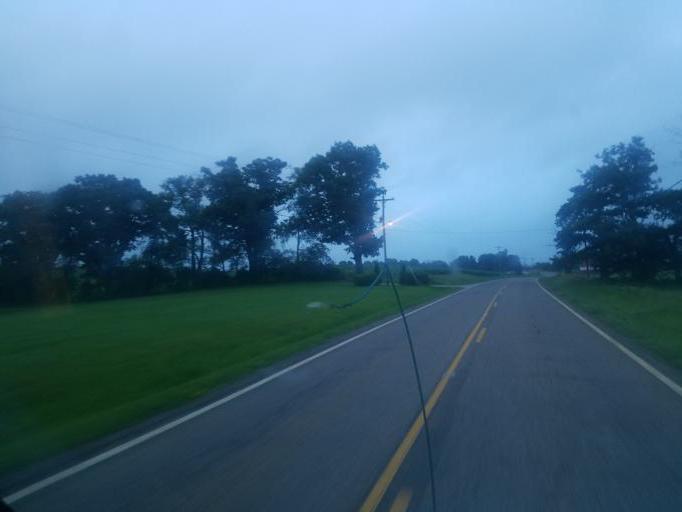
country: US
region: Ohio
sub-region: Columbiana County
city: Salineville
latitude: 40.6172
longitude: -80.9389
